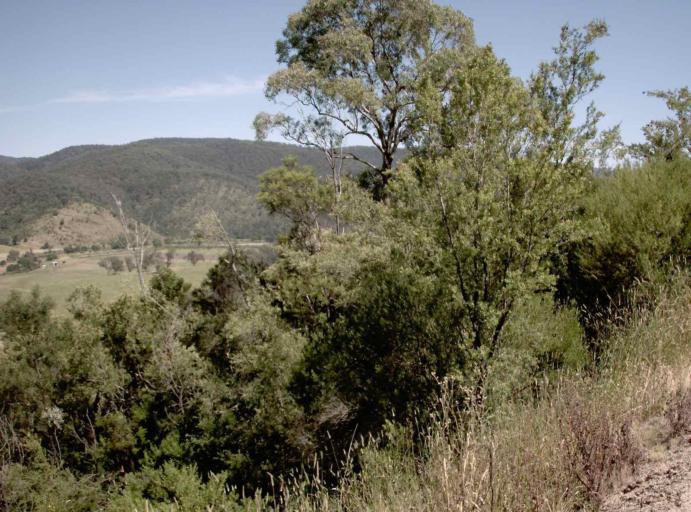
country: AU
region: Victoria
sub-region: East Gippsland
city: Lakes Entrance
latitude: -37.4878
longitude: 148.1868
